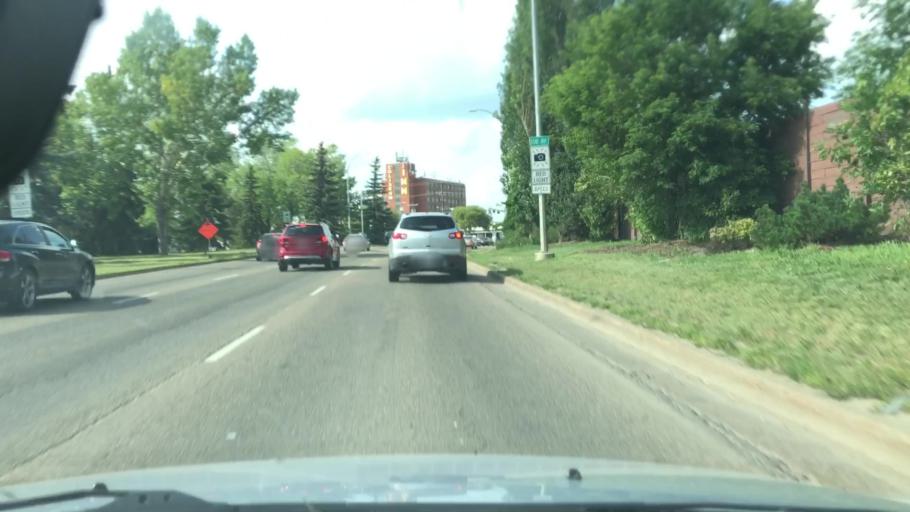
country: CA
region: Alberta
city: Edmonton
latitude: 53.5690
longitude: -113.4517
